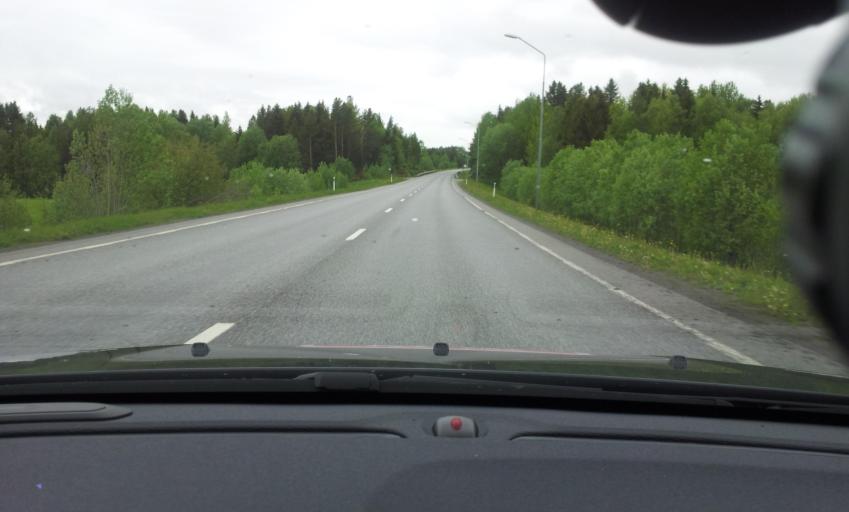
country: SE
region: Jaemtland
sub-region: Krokoms Kommun
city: Valla
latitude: 63.3225
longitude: 14.0588
